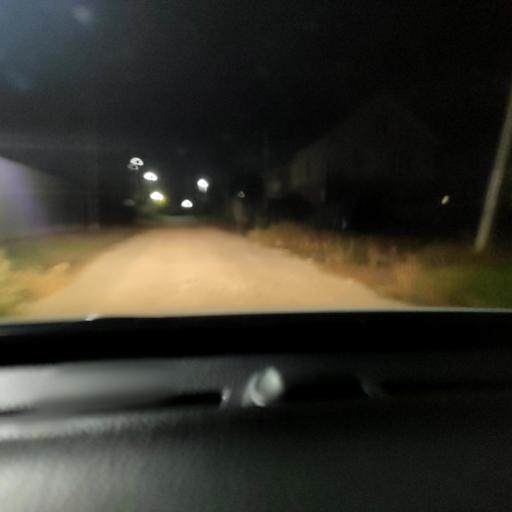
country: RU
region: Voronezj
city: Novaya Usman'
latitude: 51.6597
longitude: 39.4019
